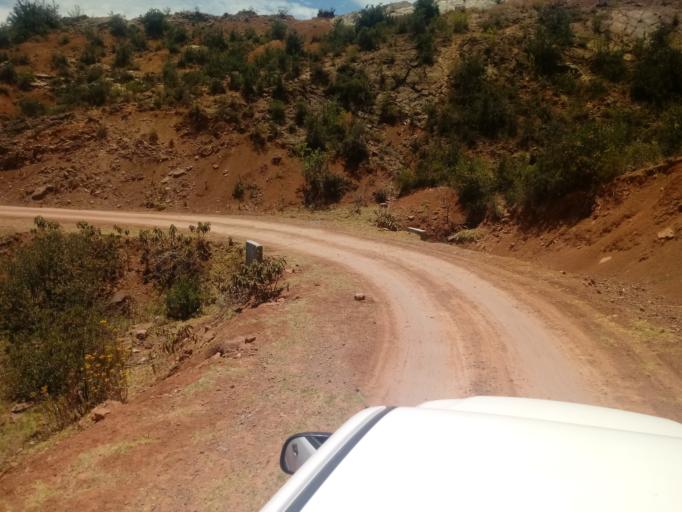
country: PE
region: Huancavelica
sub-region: Provincia de Angaraes
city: Antaparco
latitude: -13.0856
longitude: -74.3835
